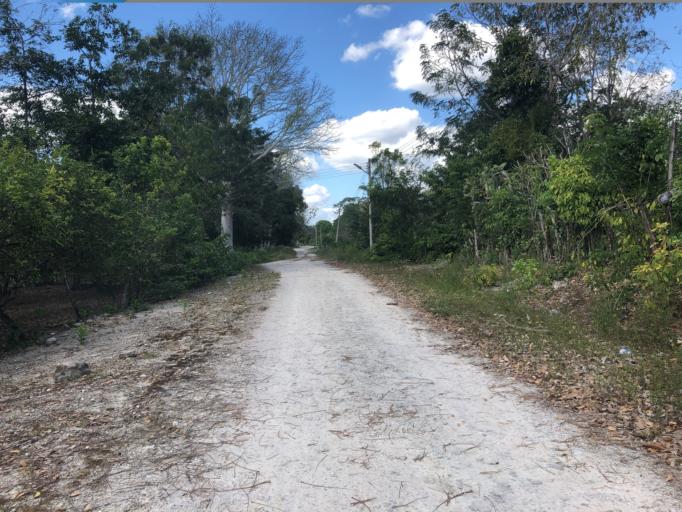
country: MX
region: Quintana Roo
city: Nicolas Bravo
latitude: 18.4486
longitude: -89.3066
